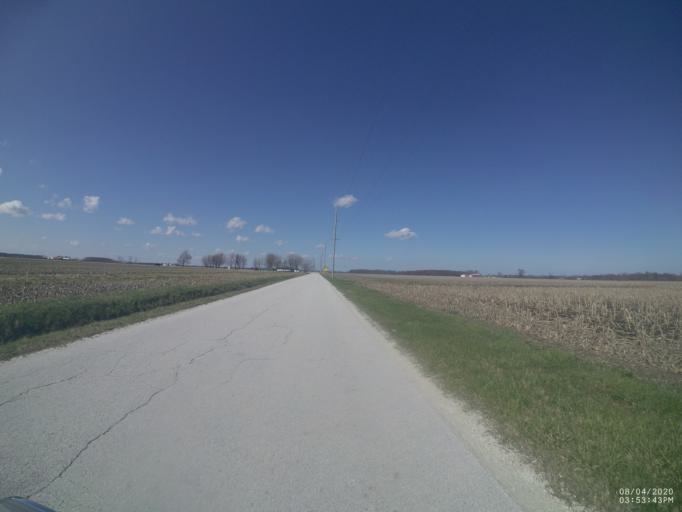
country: US
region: Ohio
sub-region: Sandusky County
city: Ballville
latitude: 41.2776
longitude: -83.1884
